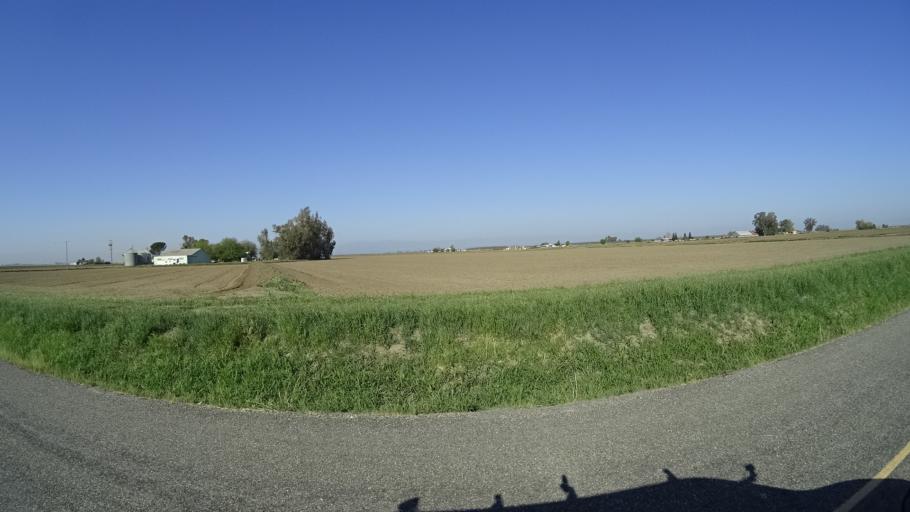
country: US
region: California
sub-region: Glenn County
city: Willows
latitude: 39.5706
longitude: -122.1075
